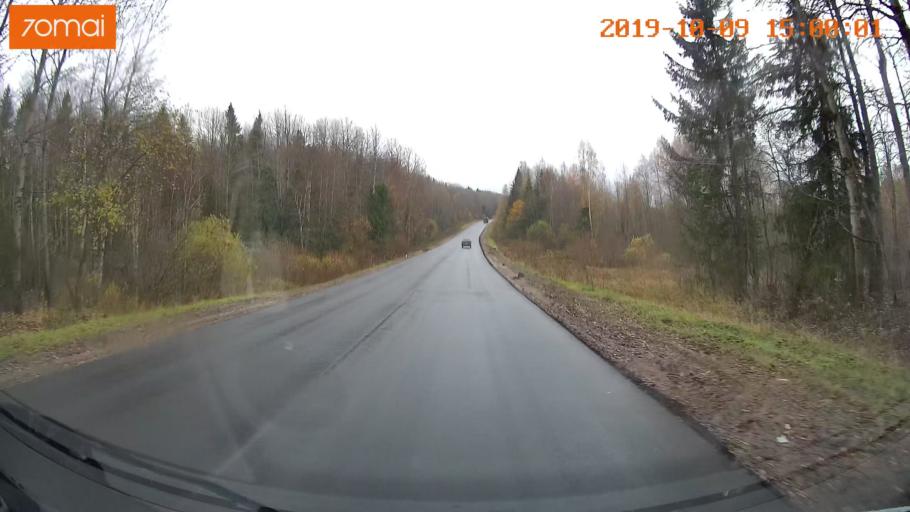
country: RU
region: Kostroma
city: Chistyye Bory
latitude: 58.3138
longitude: 41.6747
